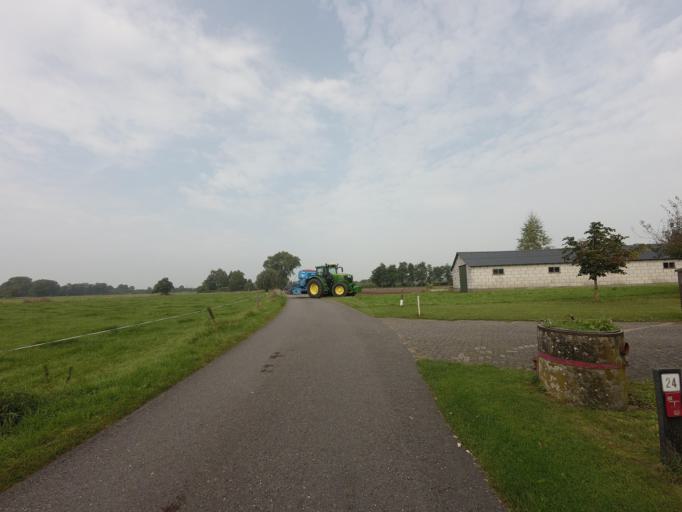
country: NL
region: Gelderland
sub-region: Gemeente Apeldoorn
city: Apeldoorn
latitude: 52.2368
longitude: 6.0261
